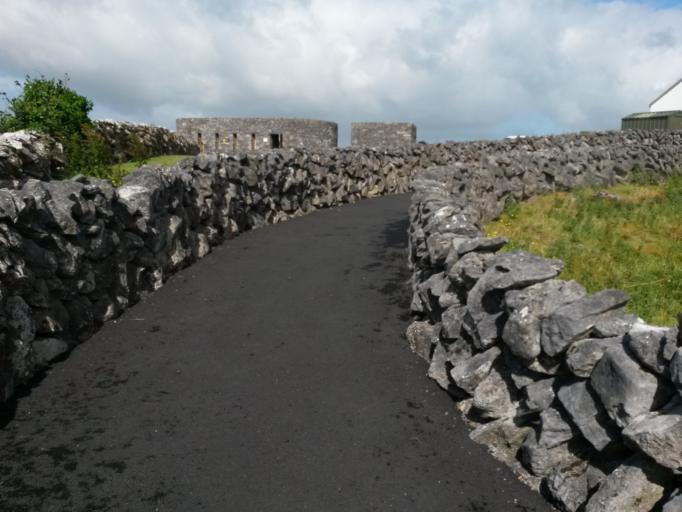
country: IE
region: Connaught
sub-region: County Galway
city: Bearna
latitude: 53.0415
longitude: -9.1383
